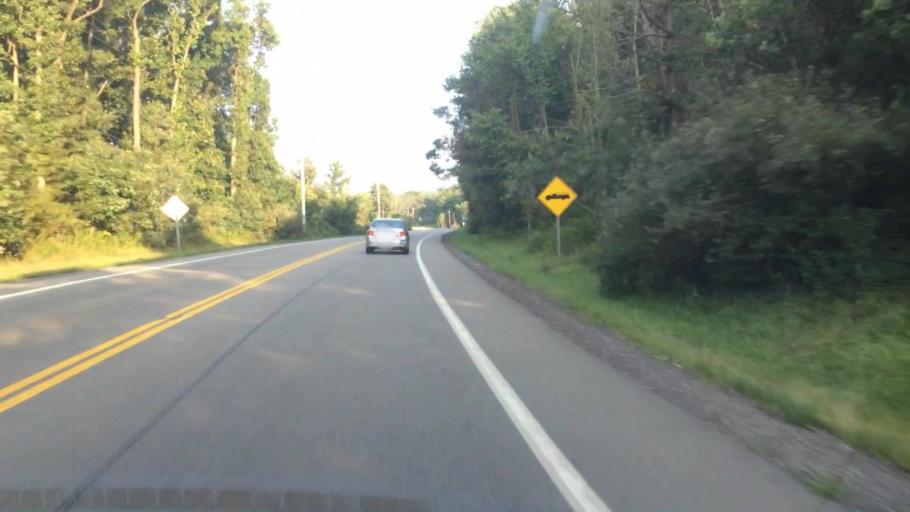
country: US
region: Ohio
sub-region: Summit County
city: Peninsula
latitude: 41.2388
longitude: -81.5380
